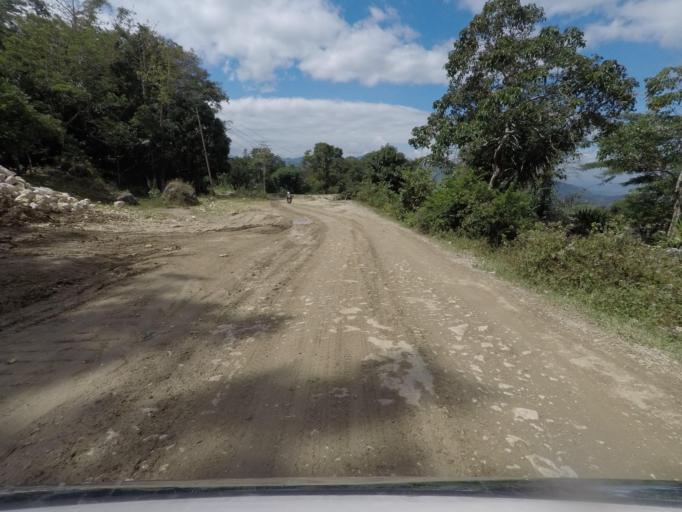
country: TL
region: Baucau
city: Venilale
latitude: -8.7344
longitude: 126.3688
